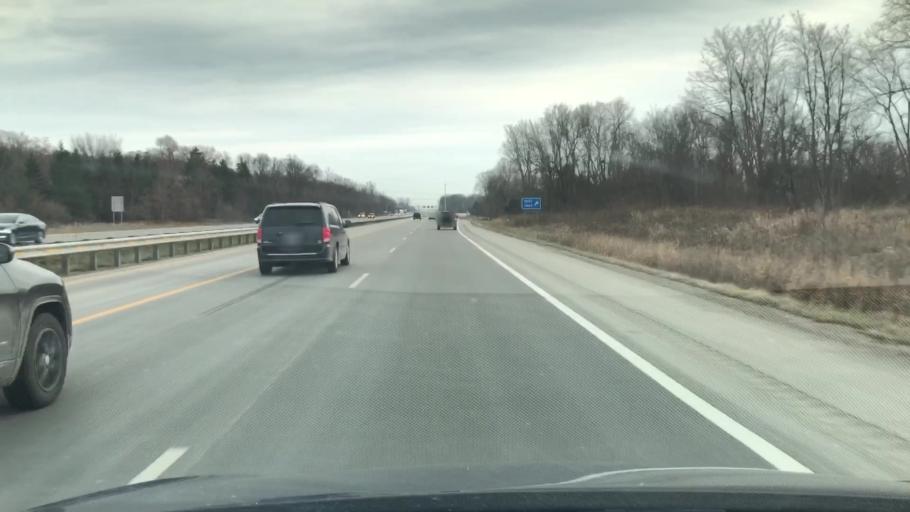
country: US
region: Michigan
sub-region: Livingston County
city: Whitmore Lake
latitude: 42.3621
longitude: -83.7493
